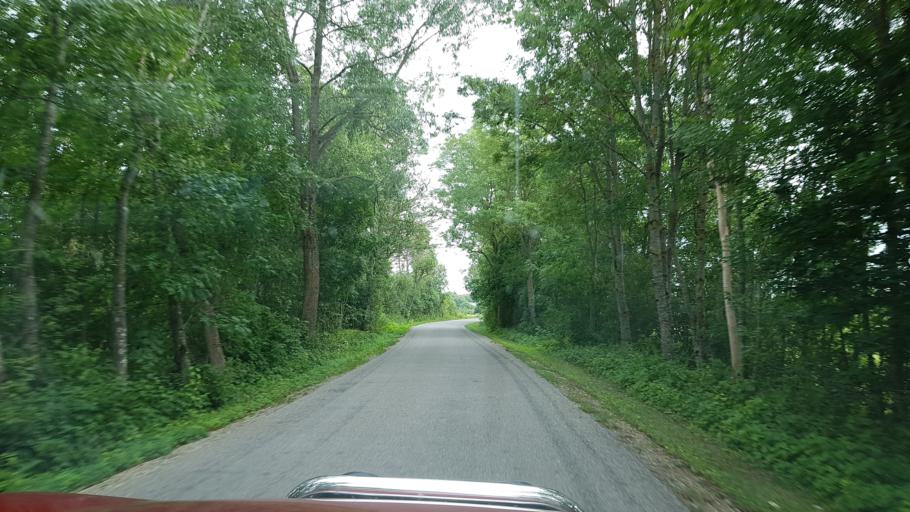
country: EE
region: Laeaene
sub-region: Ridala Parish
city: Uuemoisa
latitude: 58.9750
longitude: 23.7703
